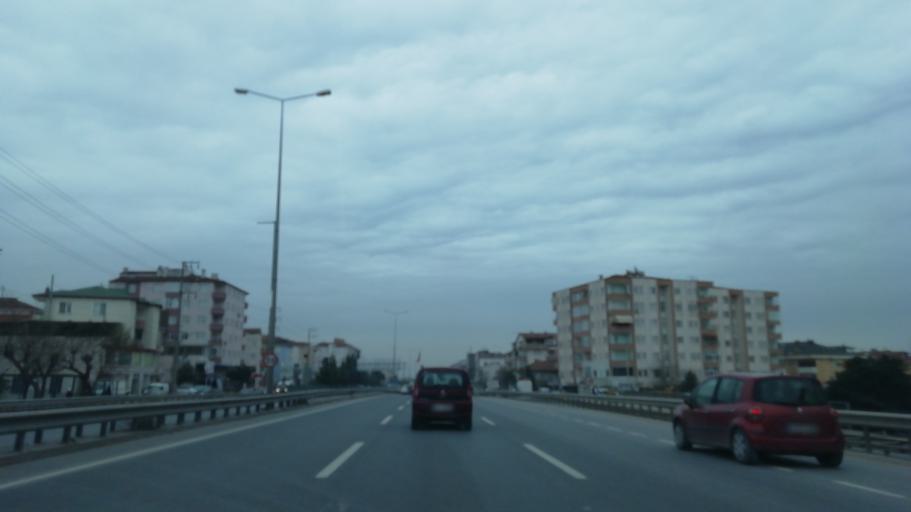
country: TR
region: Kocaeli
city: Derince
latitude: 40.7562
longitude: 29.8237
